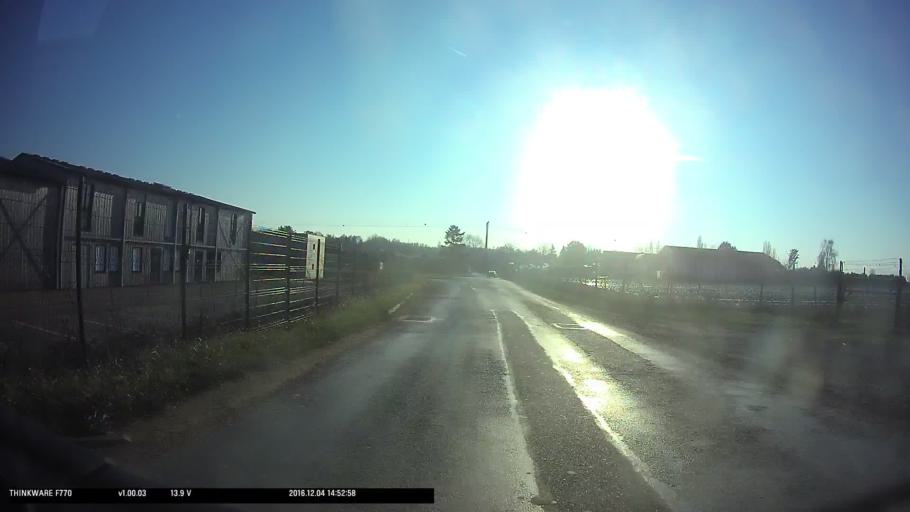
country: FR
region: Ile-de-France
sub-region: Departement du Val-d'Oise
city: Courdimanche
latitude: 49.0625
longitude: 2.0018
